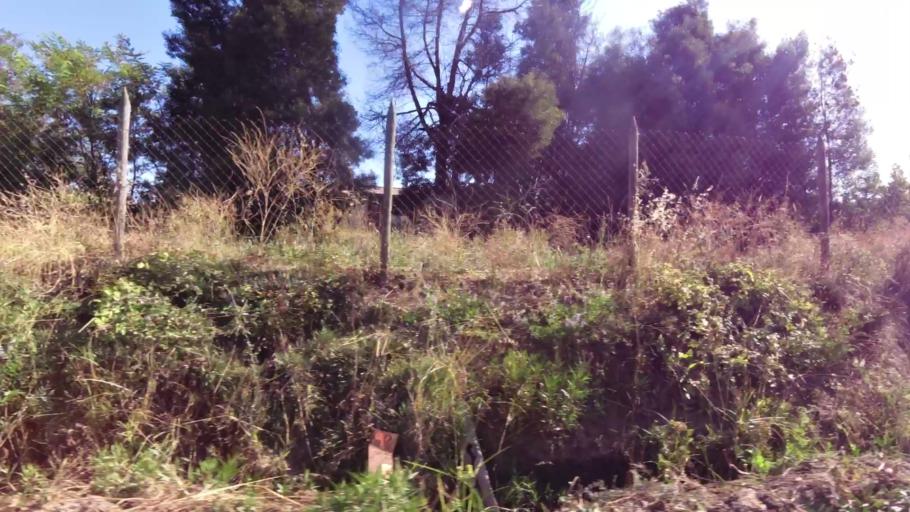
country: CL
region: Maule
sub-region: Provincia de Talca
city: Talca
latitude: -35.4029
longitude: -71.6066
